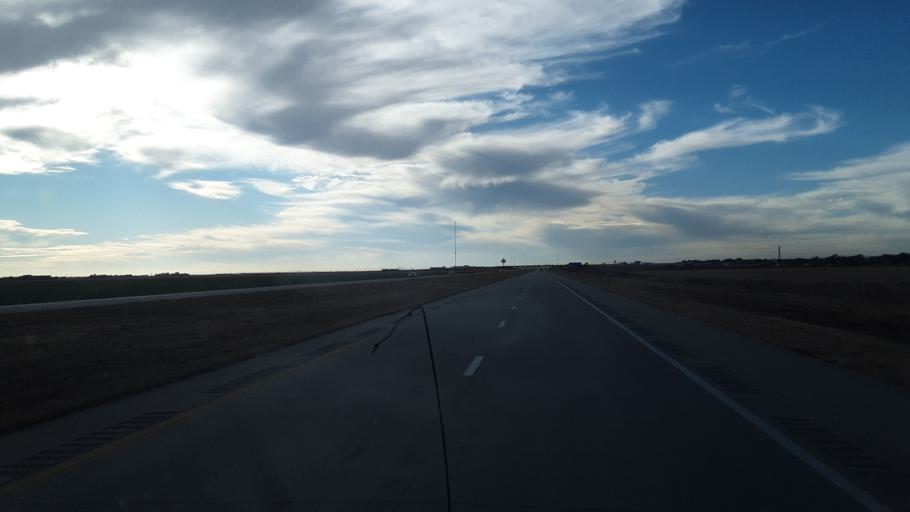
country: US
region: Kansas
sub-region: Finney County
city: Holcomb
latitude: 38.0034
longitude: -100.9767
